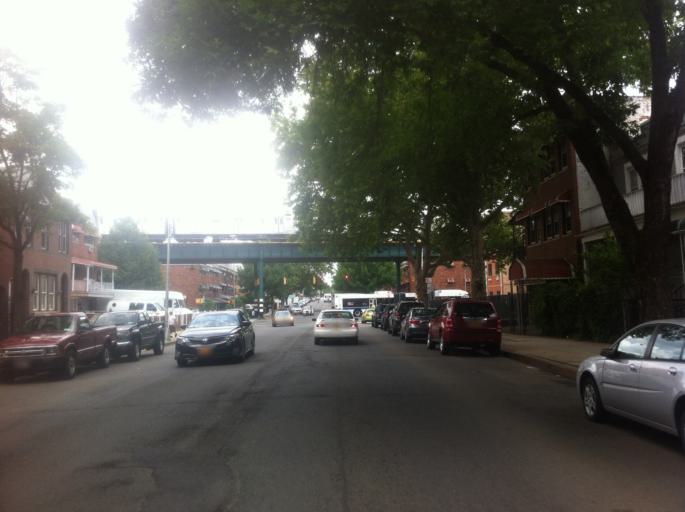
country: US
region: New York
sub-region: Bronx
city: The Bronx
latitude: 40.8303
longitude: -73.8689
